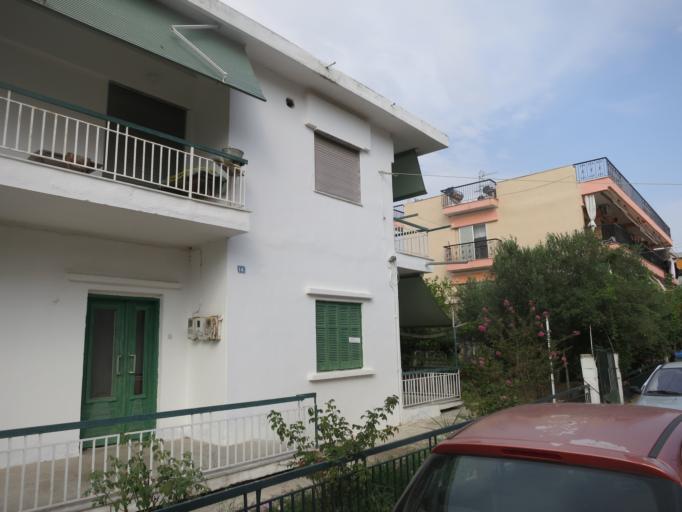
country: GR
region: Central Macedonia
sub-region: Nomos Chalkidikis
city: Nea Flogita
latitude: 40.2512
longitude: 23.2478
